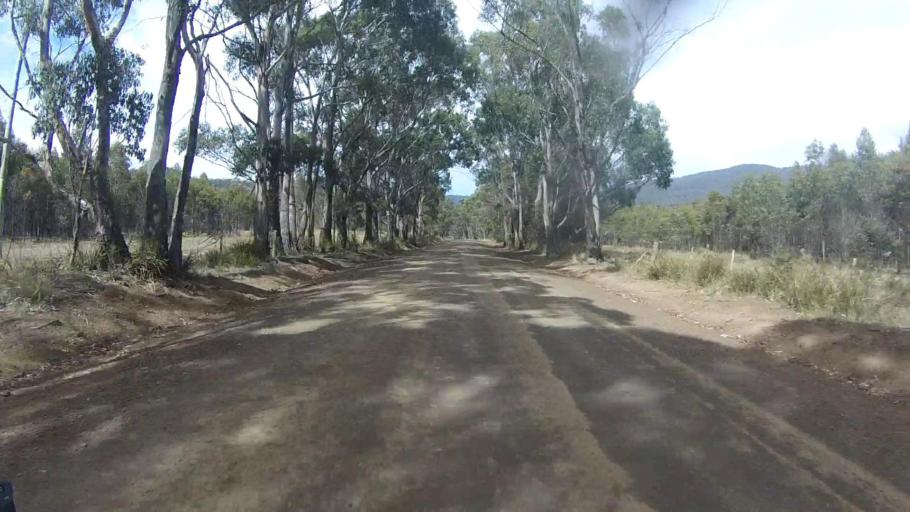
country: AU
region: Tasmania
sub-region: Sorell
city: Sorell
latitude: -42.6602
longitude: 147.8954
